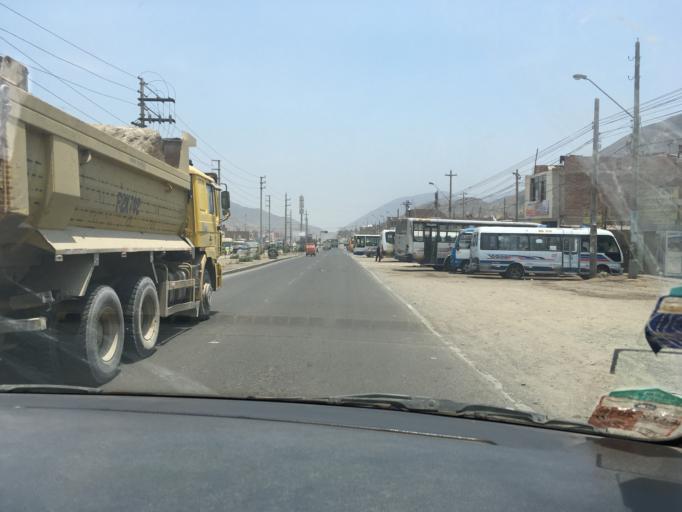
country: PE
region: Lima
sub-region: Lima
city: Cieneguilla
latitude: -12.1213
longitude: -76.8727
